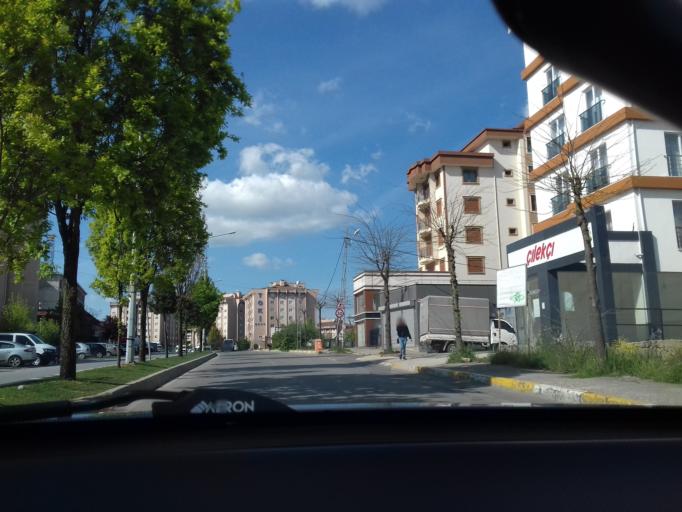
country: TR
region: Istanbul
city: Pendik
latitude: 40.9070
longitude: 29.2786
